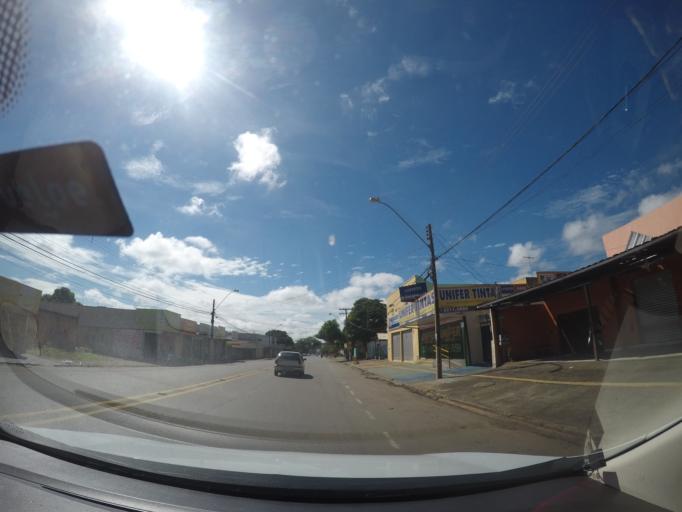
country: BR
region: Goias
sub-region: Goiania
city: Goiania
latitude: -16.6198
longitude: -49.2893
